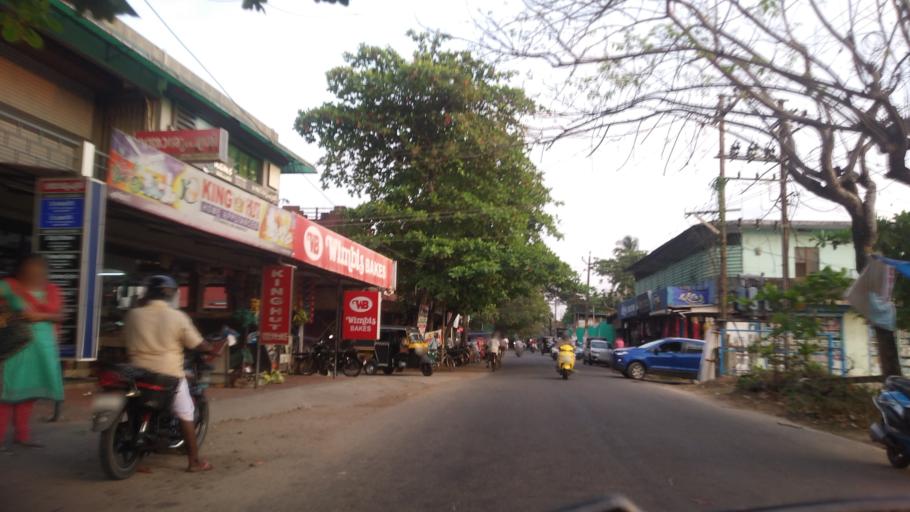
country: IN
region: Kerala
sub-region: Thrissur District
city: Kodungallur
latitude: 10.2247
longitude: 76.1567
